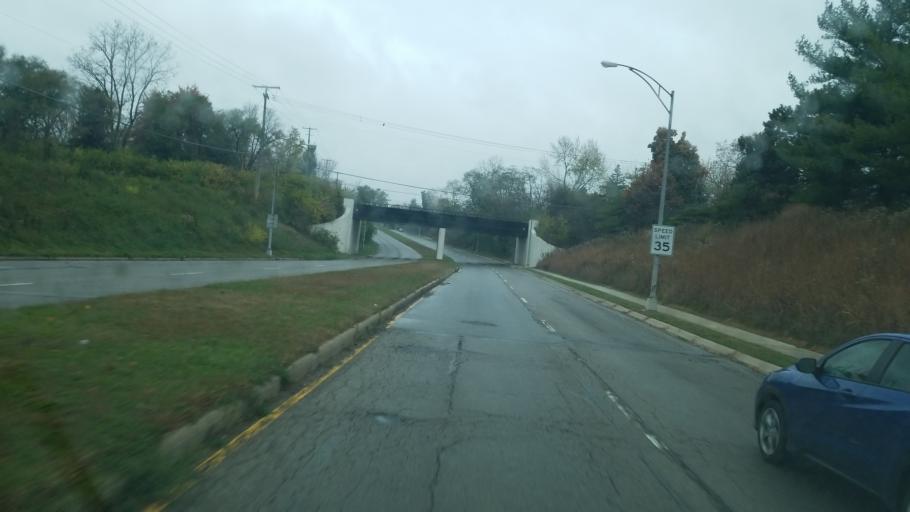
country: US
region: Ohio
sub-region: Franklin County
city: Upper Arlington
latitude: 40.0295
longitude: -83.0369
